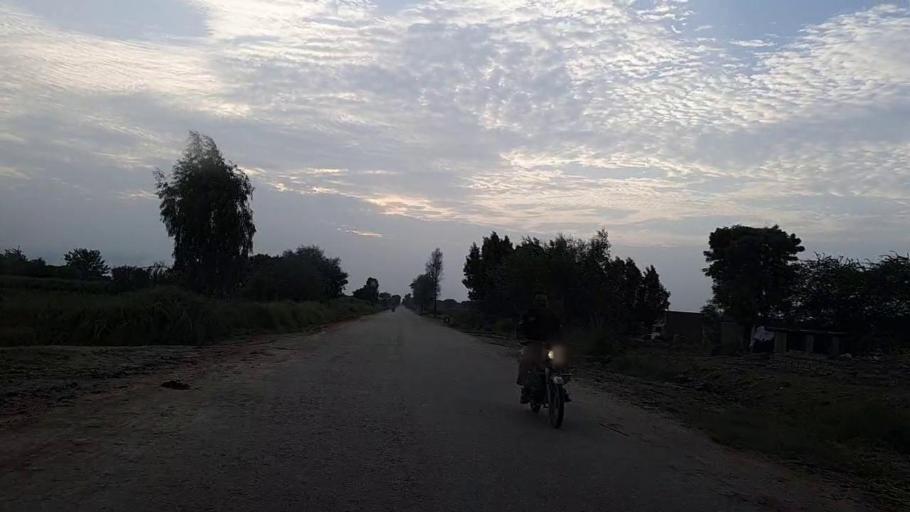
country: PK
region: Sindh
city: Pad Idan
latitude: 26.7987
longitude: 68.2310
